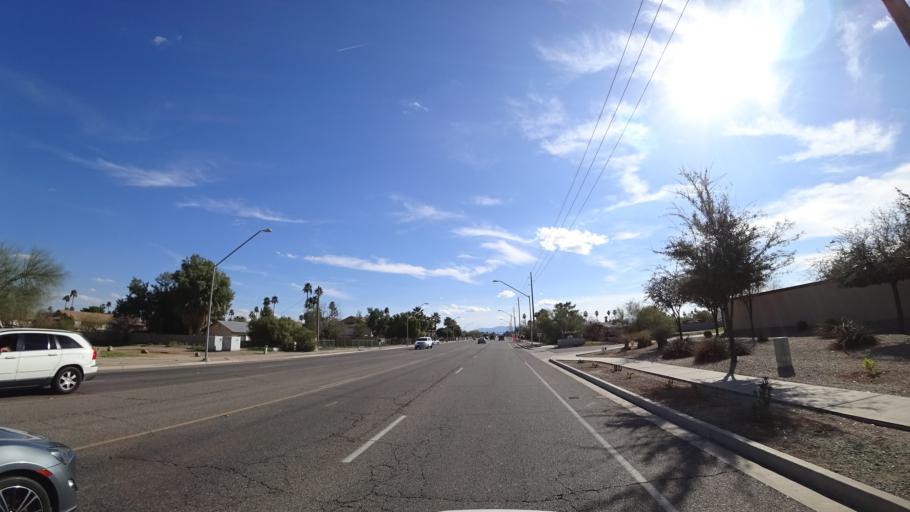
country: US
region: Arizona
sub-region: Maricopa County
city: Glendale
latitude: 33.5420
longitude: -112.2205
